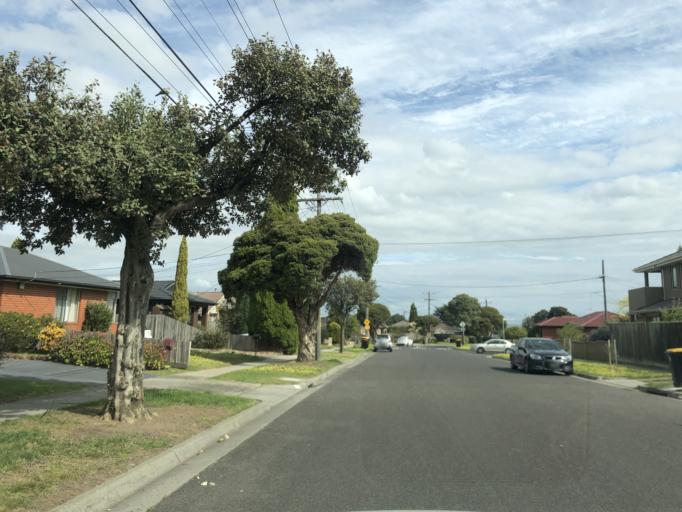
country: AU
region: Victoria
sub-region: Greater Dandenong
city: Noble Park North
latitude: -37.9532
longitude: 145.1995
